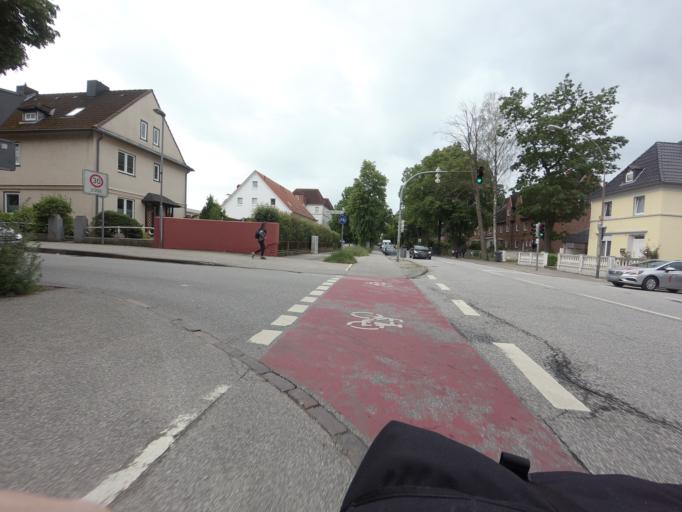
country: DE
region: Mecklenburg-Vorpommern
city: Selmsdorf
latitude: 53.9056
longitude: 10.8033
